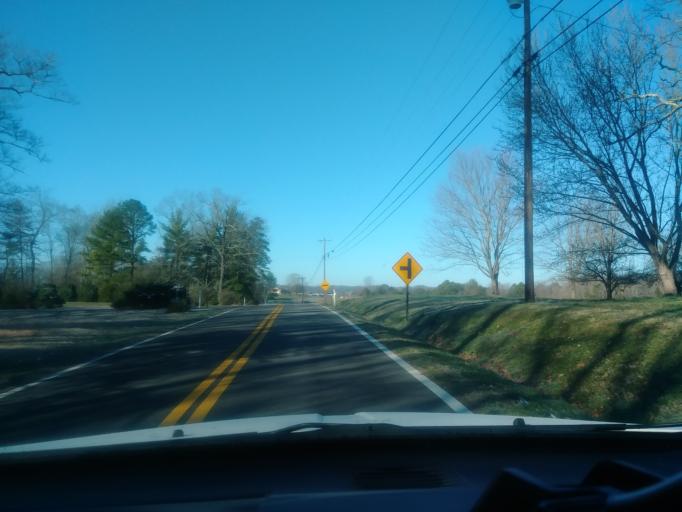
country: US
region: Tennessee
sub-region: Greene County
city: Mosheim
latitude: 36.1178
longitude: -82.9793
